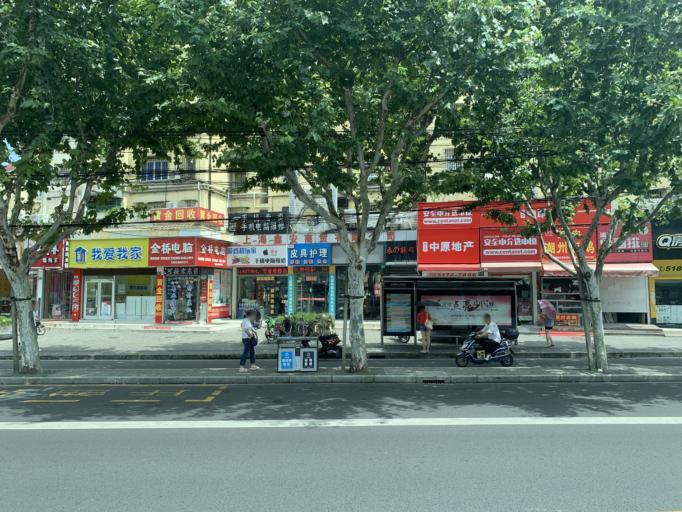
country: CN
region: Shanghai Shi
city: Pudong
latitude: 31.2516
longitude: 121.5761
